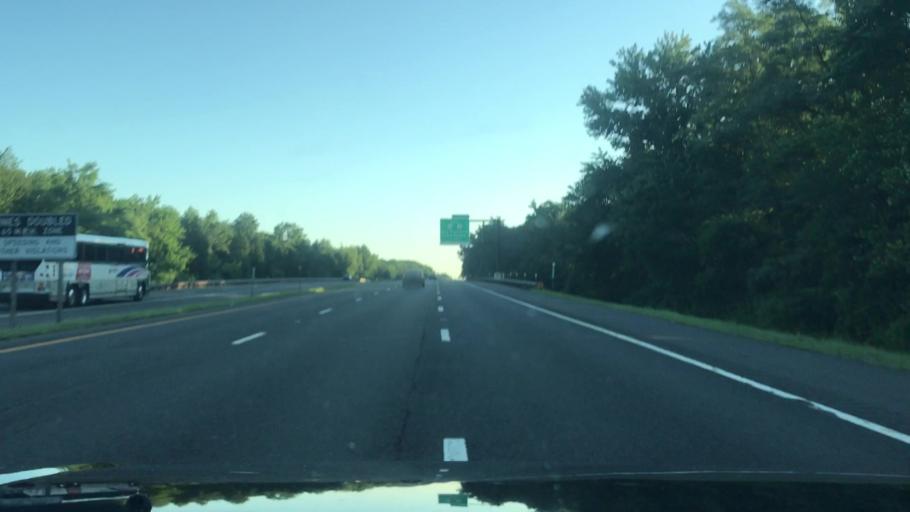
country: US
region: New Jersey
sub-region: Monmouth County
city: Eatontown
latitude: 40.2562
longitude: -74.0797
